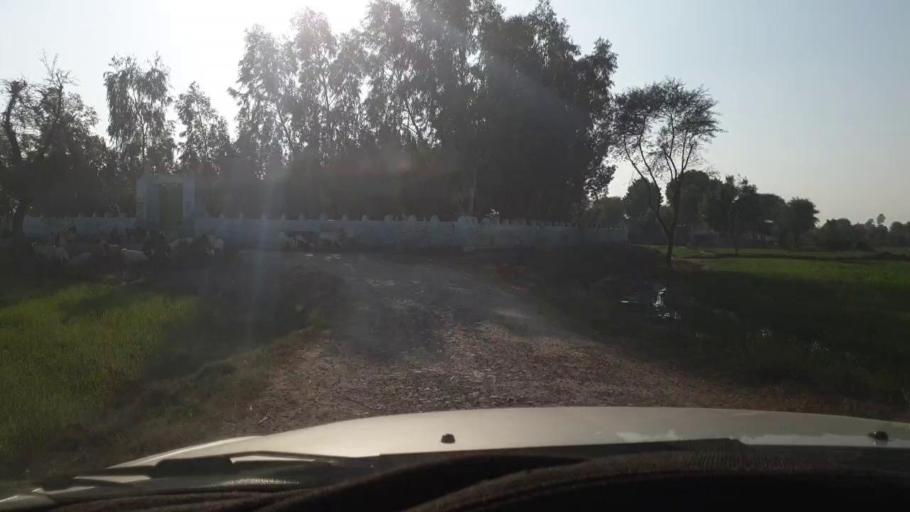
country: PK
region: Sindh
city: Mirpur Mathelo
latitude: 28.0181
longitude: 69.6010
